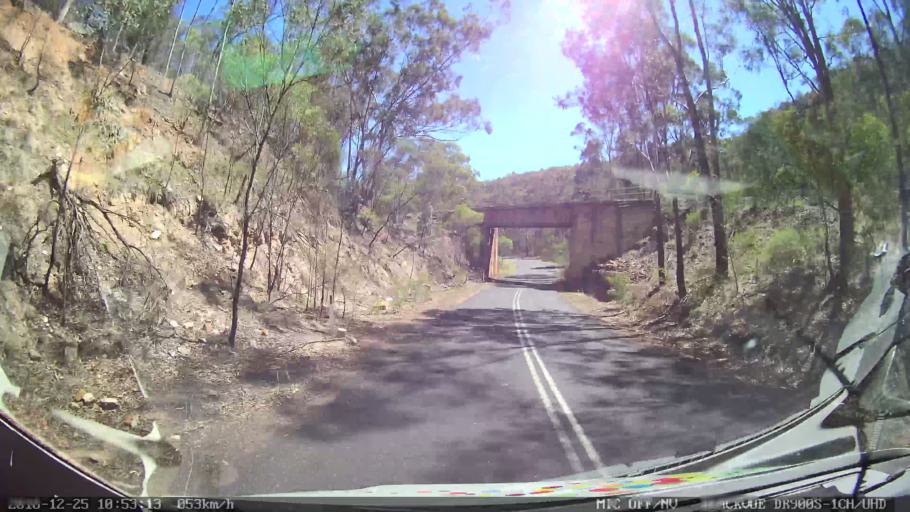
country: AU
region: New South Wales
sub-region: Upper Hunter Shire
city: Merriwa
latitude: -32.4219
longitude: 150.2729
